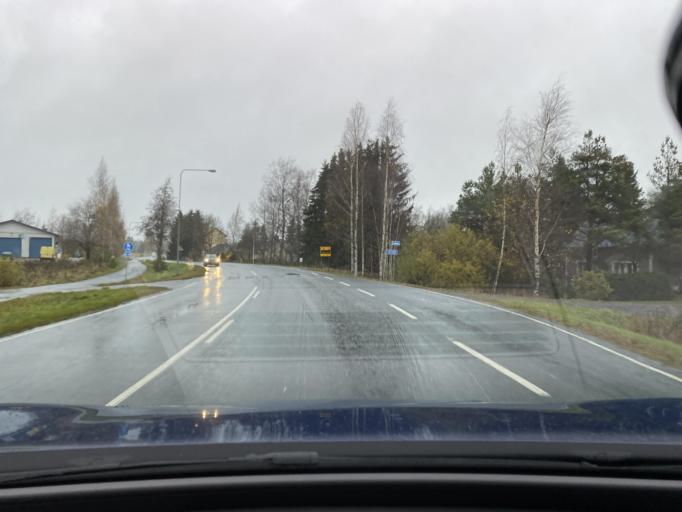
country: FI
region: Varsinais-Suomi
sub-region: Loimaa
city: Alastaro
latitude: 60.9410
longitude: 22.8702
